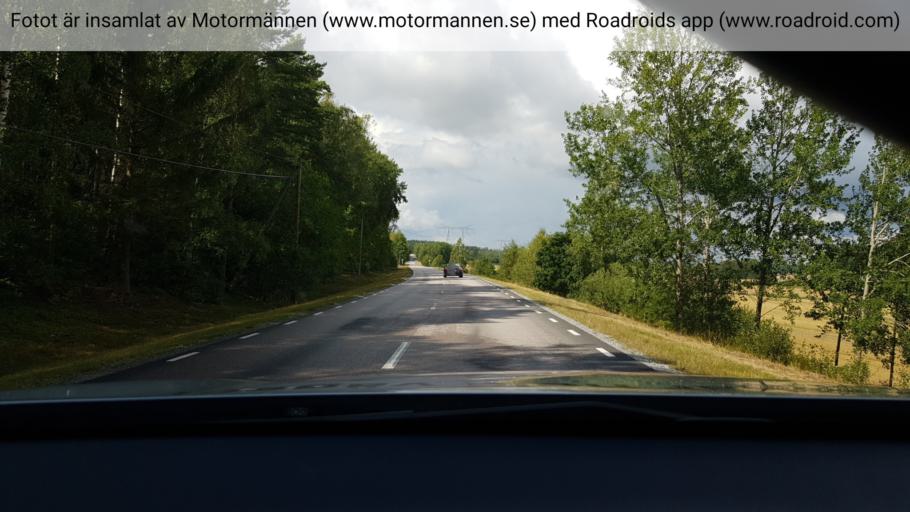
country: SE
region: Stockholm
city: Stenhamra
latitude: 59.3686
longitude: 17.6095
